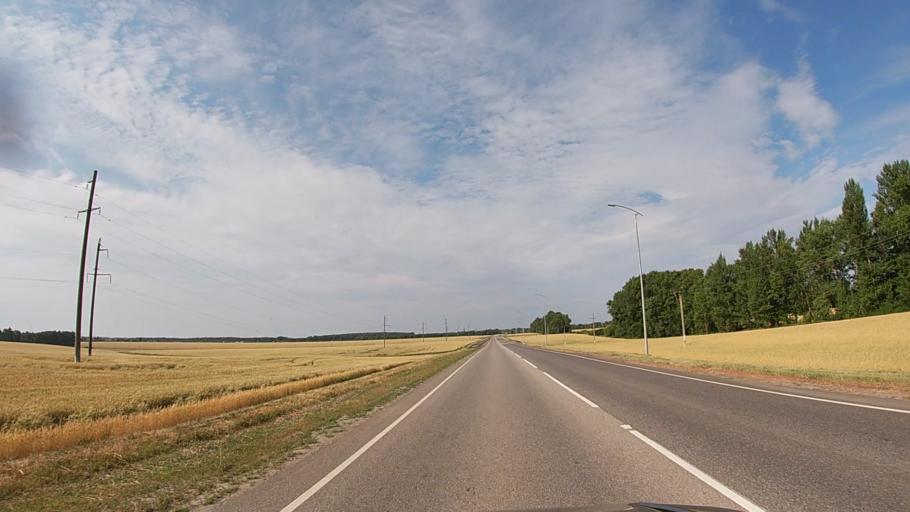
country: RU
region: Belgorod
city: Proletarskiy
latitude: 50.8129
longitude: 35.7493
